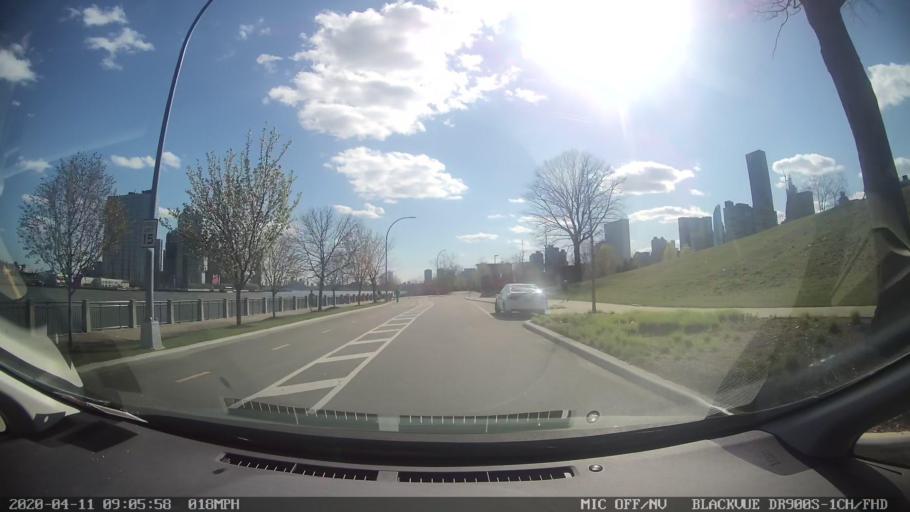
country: US
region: New York
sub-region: Queens County
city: Long Island City
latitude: 40.7538
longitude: -73.9562
